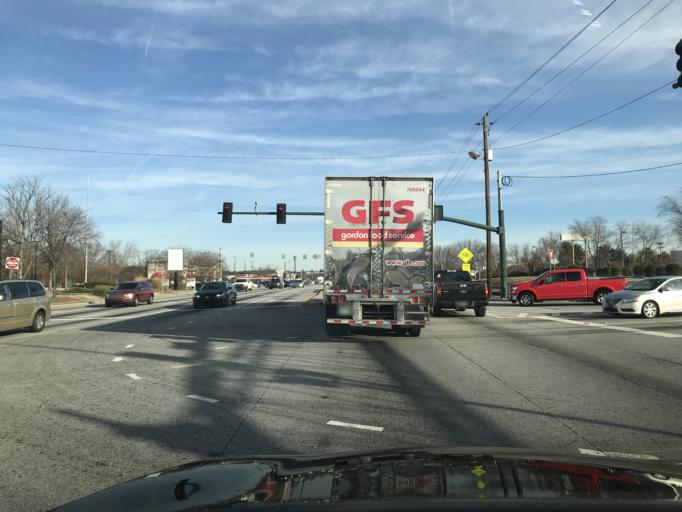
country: US
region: Georgia
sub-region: Clayton County
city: Morrow
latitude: 33.5712
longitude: -84.3426
